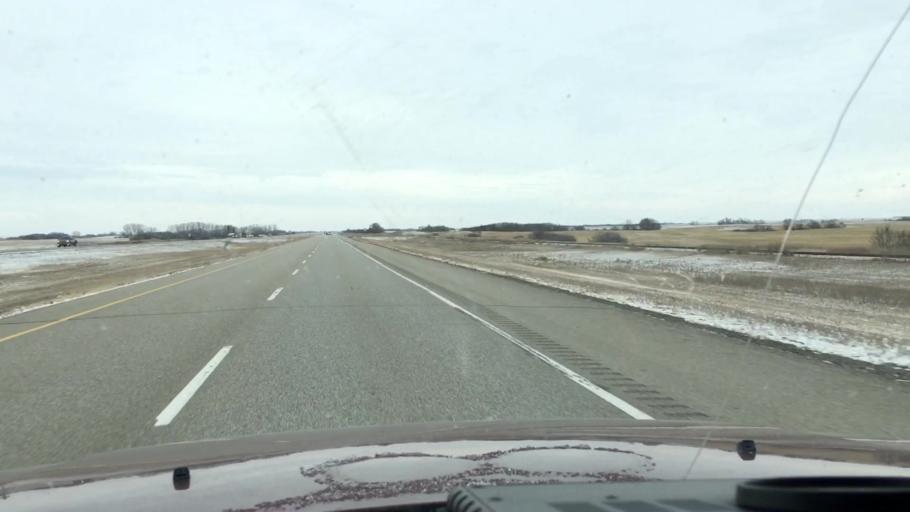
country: CA
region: Saskatchewan
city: Watrous
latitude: 51.3492
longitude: -106.1148
